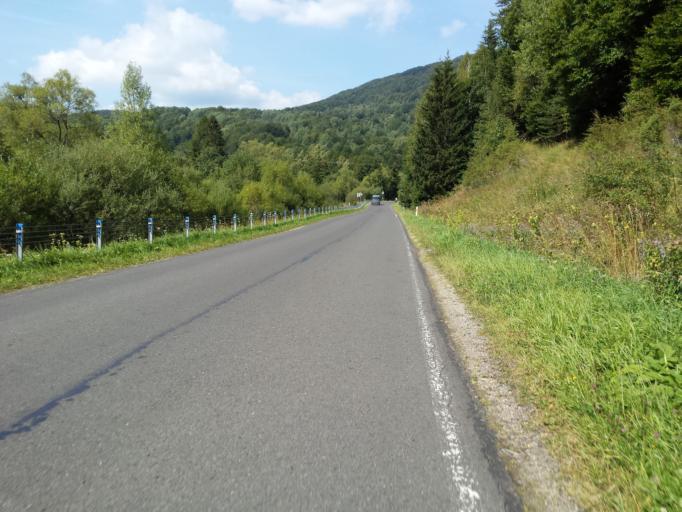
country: PL
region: Subcarpathian Voivodeship
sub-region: Powiat bieszczadzki
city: Lutowiska
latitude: 49.1393
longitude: 22.5704
